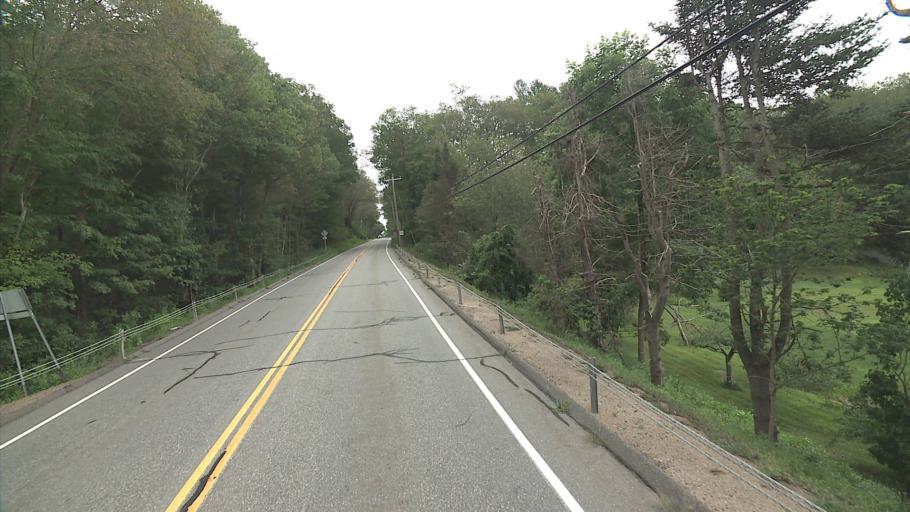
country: US
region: Connecticut
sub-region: Tolland County
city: Storrs
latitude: 41.8738
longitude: -72.2359
